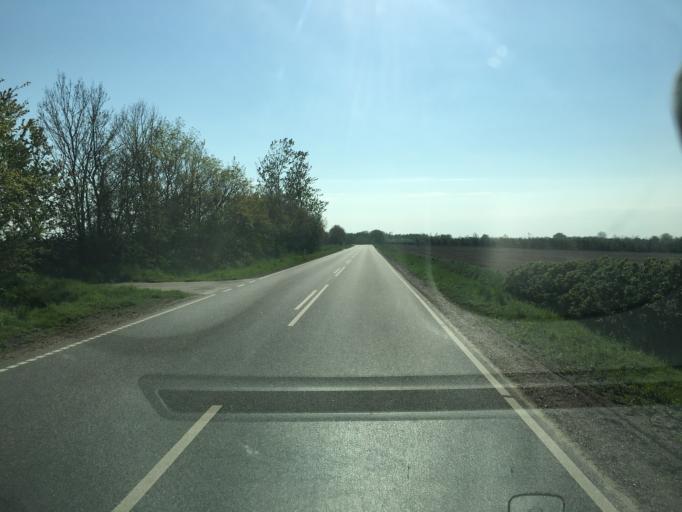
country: DK
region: South Denmark
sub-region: Tonder Kommune
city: Toftlund
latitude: 55.2015
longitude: 9.1299
